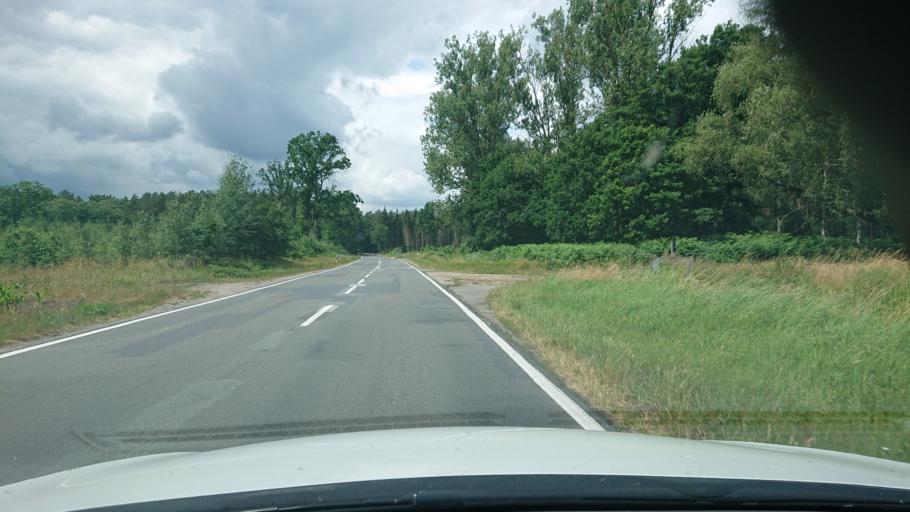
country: DE
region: Mecklenburg-Vorpommern
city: Ludwigslust
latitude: 53.3591
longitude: 11.4803
